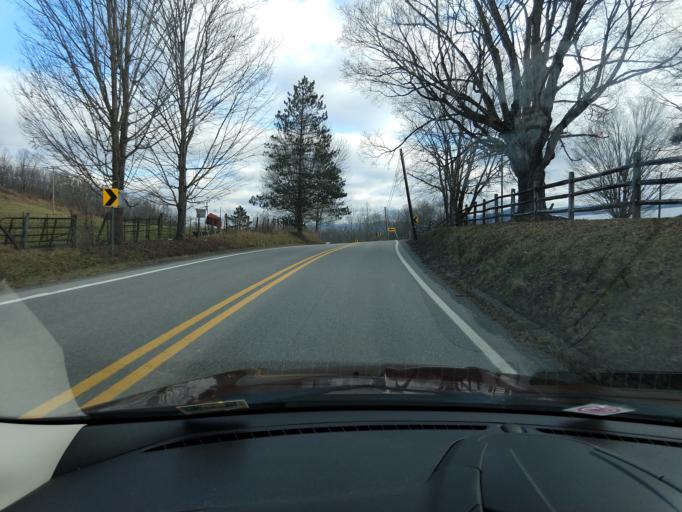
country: US
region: West Virginia
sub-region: Randolph County
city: Elkins
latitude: 38.7811
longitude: -79.9129
